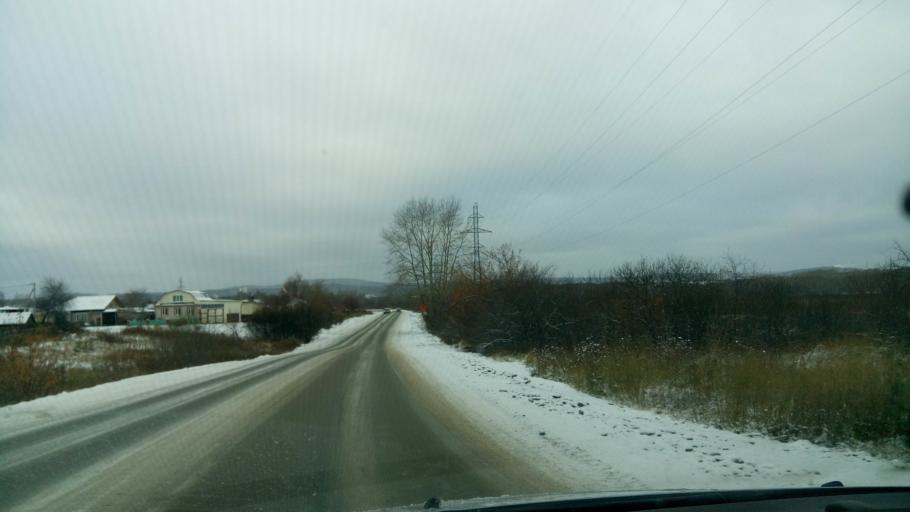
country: RU
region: Sverdlovsk
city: Polevskoy
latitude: 56.4575
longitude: 60.2057
